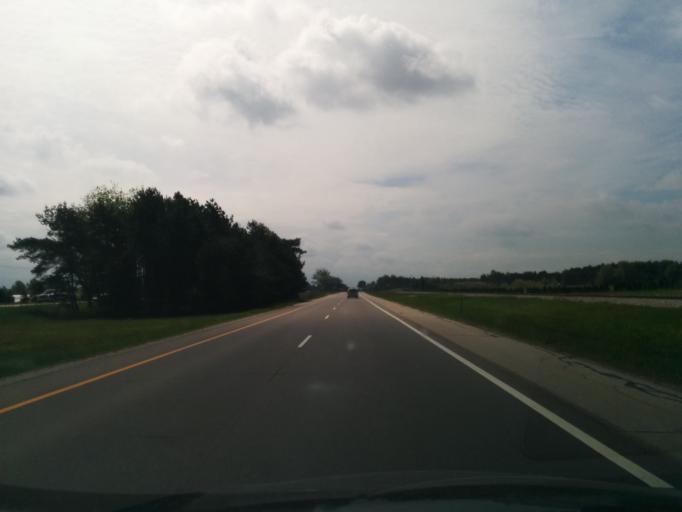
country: US
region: Michigan
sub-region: Ottawa County
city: Grand Haven
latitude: 42.9474
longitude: -86.1648
